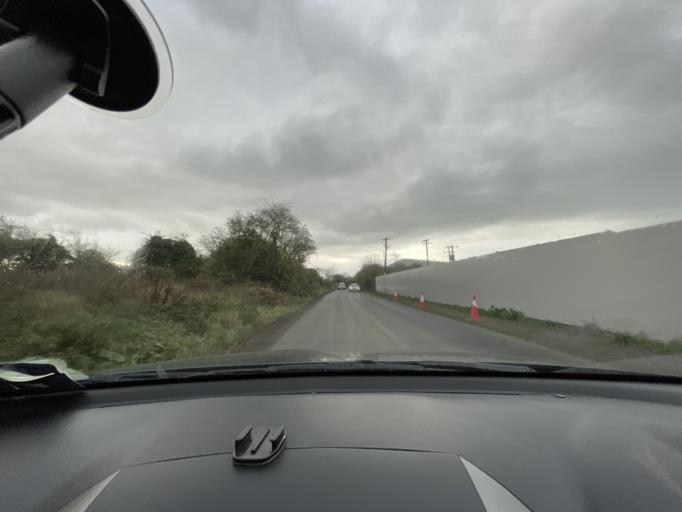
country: IE
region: Leinster
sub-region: Lu
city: Drogheda
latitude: 53.7261
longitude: -6.3194
